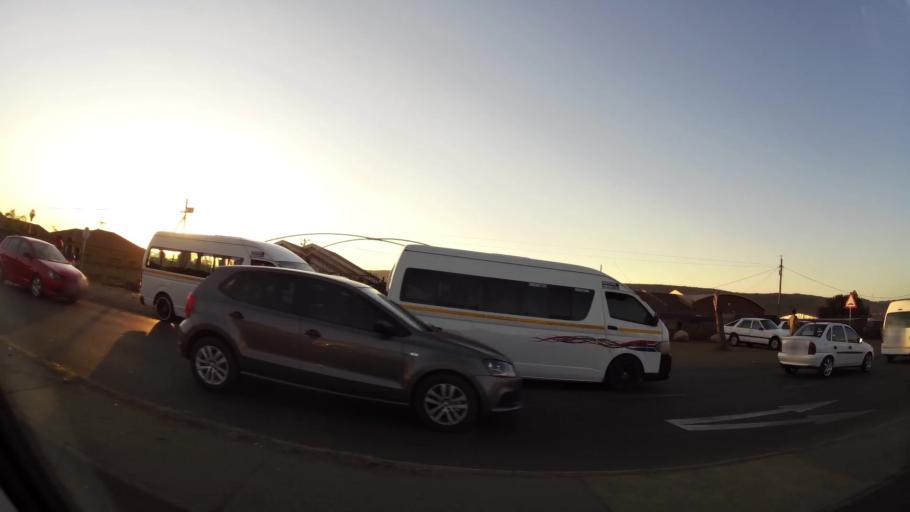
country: ZA
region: Gauteng
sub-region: City of Tshwane Metropolitan Municipality
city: Cullinan
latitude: -25.7187
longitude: 28.3656
